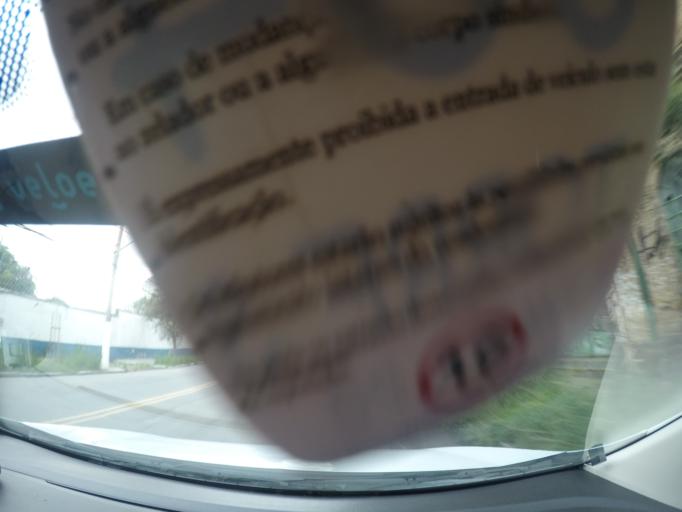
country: BR
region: Sao Paulo
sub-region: Sao Paulo
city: Sao Paulo
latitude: -23.5562
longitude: -46.6117
